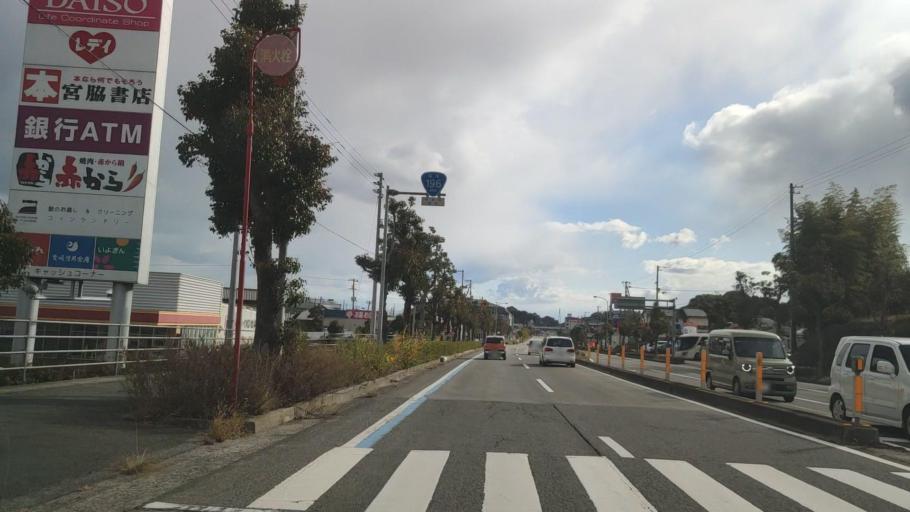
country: JP
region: Ehime
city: Hojo
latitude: 34.0609
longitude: 132.9644
